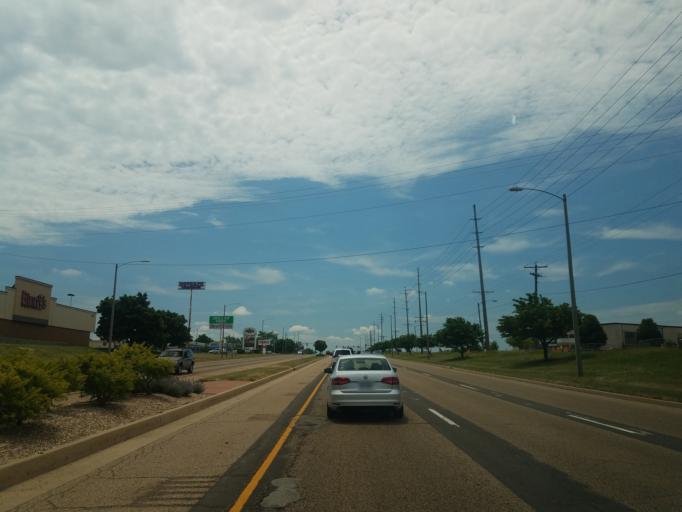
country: US
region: Illinois
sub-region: McLean County
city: Normal
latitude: 40.4998
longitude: -88.9531
